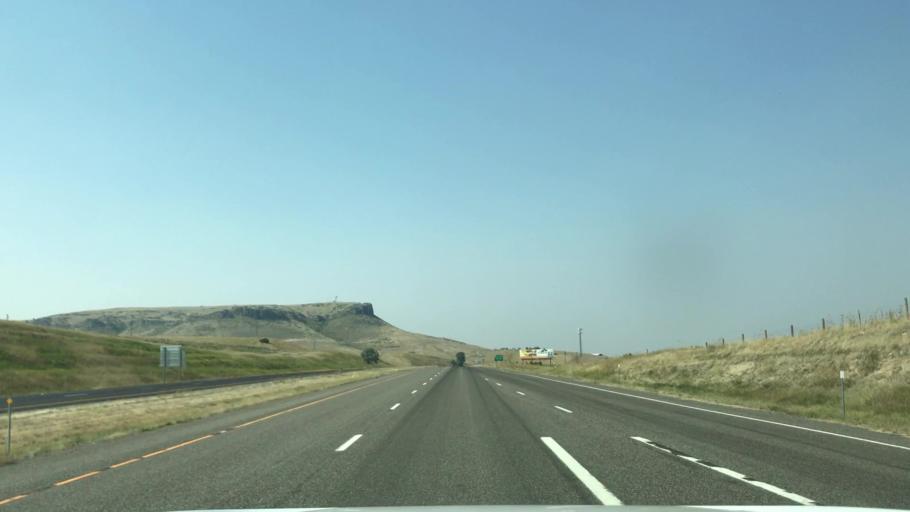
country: US
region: Montana
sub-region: Cascade County
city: Sun Prairie
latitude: 47.2641
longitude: -111.7079
